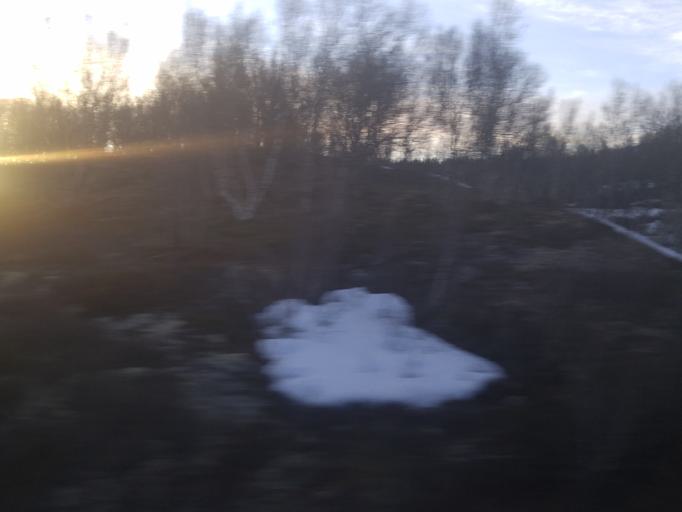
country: NO
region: Oppland
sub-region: Dovre
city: Dovre
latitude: 62.1605
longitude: 9.3424
